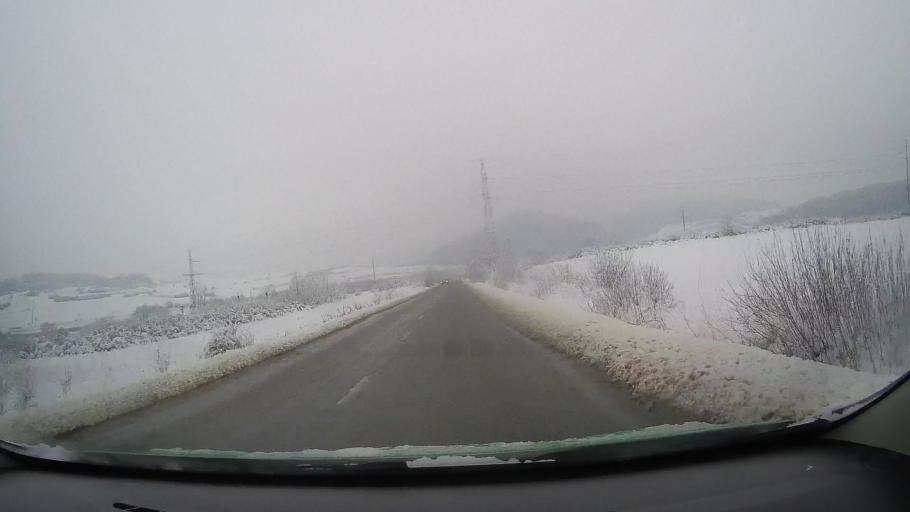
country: RO
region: Sibiu
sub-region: Comuna Orlat
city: Orlat
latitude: 45.7757
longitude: 23.9455
